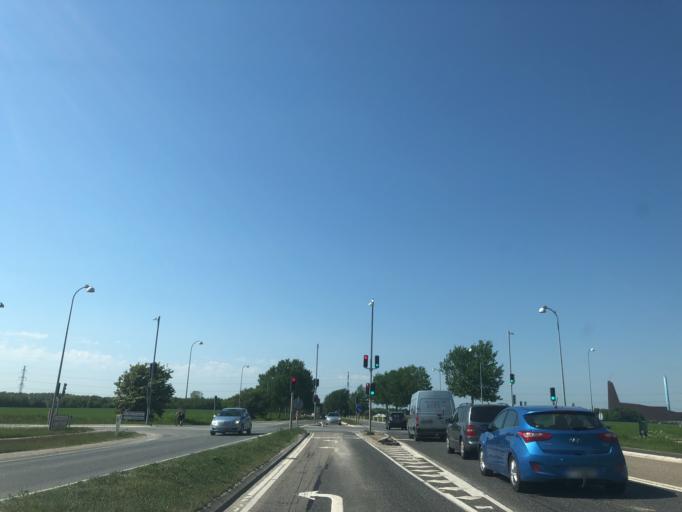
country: DK
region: Zealand
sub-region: Roskilde Kommune
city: Vindinge
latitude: 55.6273
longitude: 12.1247
